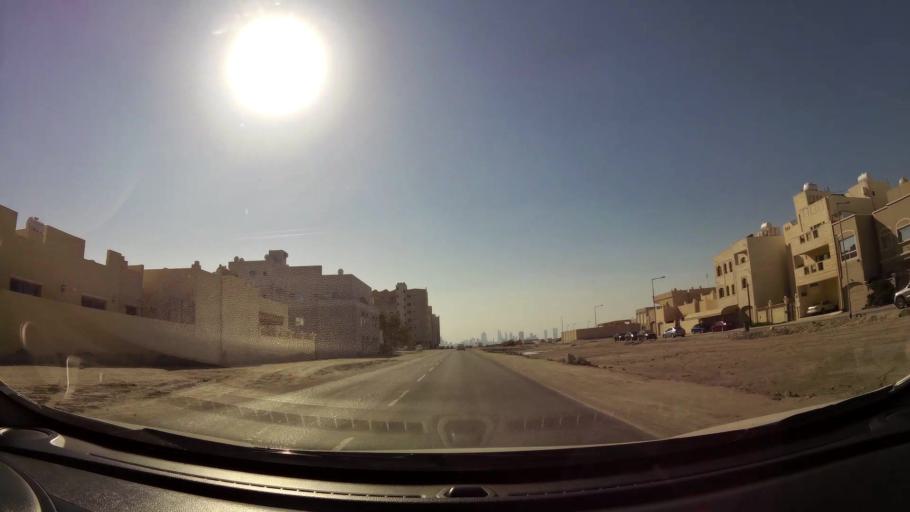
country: BH
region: Muharraq
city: Al Hadd
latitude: 26.2340
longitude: 50.6494
